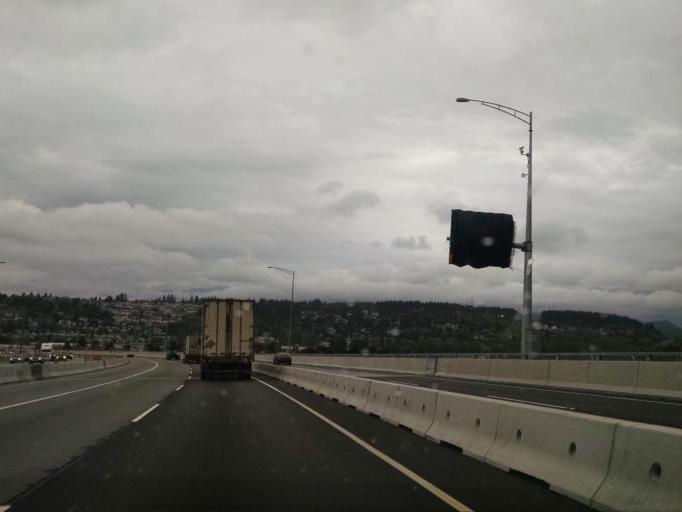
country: CA
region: British Columbia
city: Port Moody
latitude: 49.2236
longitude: -122.8148
